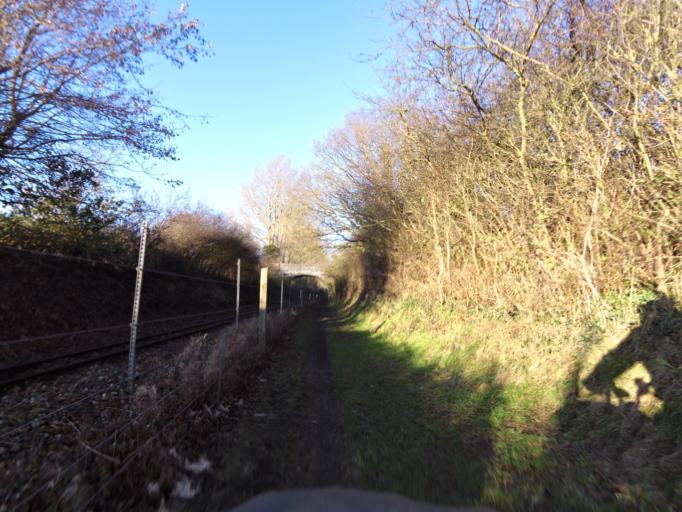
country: GB
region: England
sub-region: Norfolk
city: Aylsham
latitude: 52.7696
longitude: 1.2871
